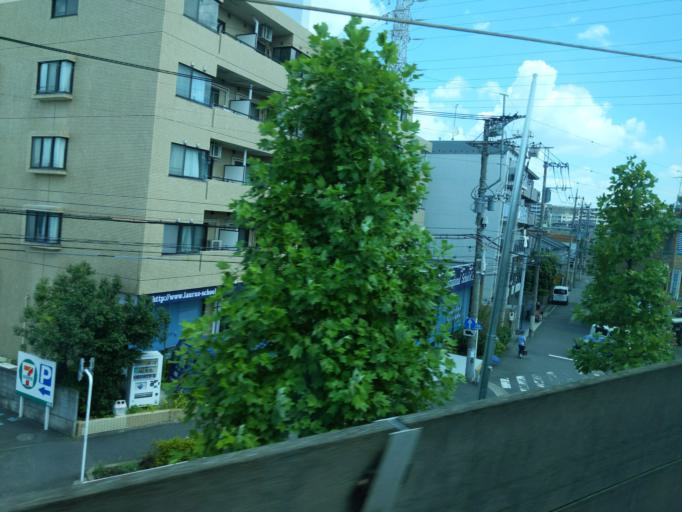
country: JP
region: Tokyo
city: Chofugaoka
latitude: 35.5887
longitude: 139.6265
